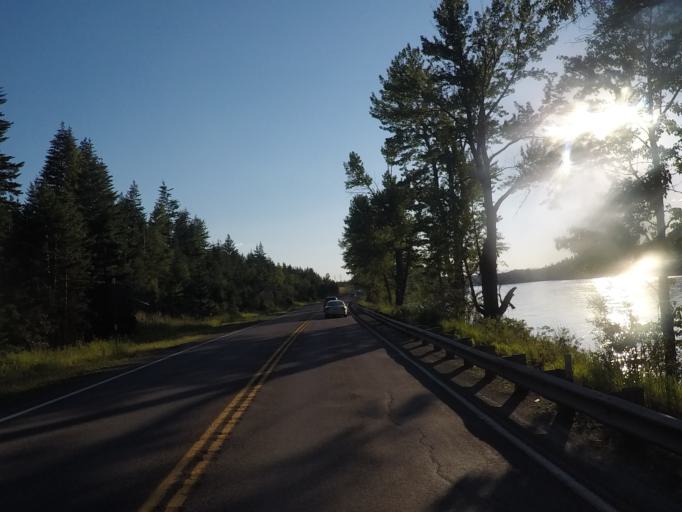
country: US
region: Montana
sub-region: Flathead County
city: Columbia Falls
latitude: 48.3849
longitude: -114.1100
